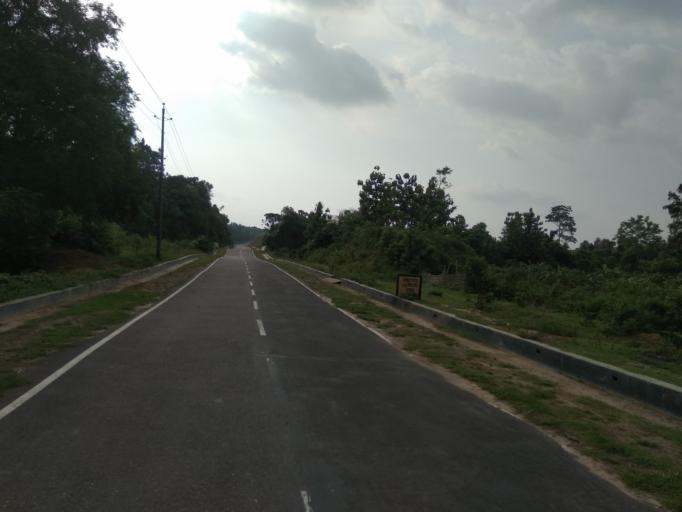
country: BD
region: Chittagong
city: Manikchari
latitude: 22.9359
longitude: 91.9088
